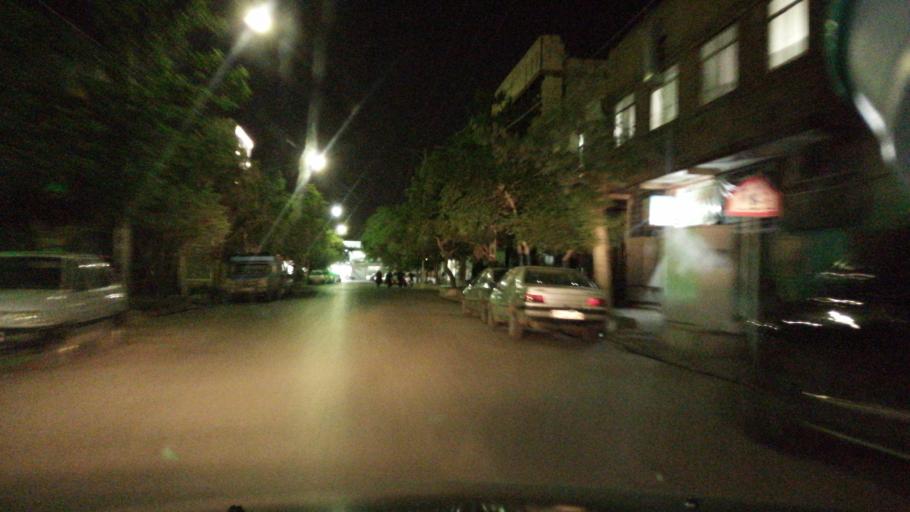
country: IR
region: Razavi Khorasan
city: Mashhad
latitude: 36.3067
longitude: 59.6037
